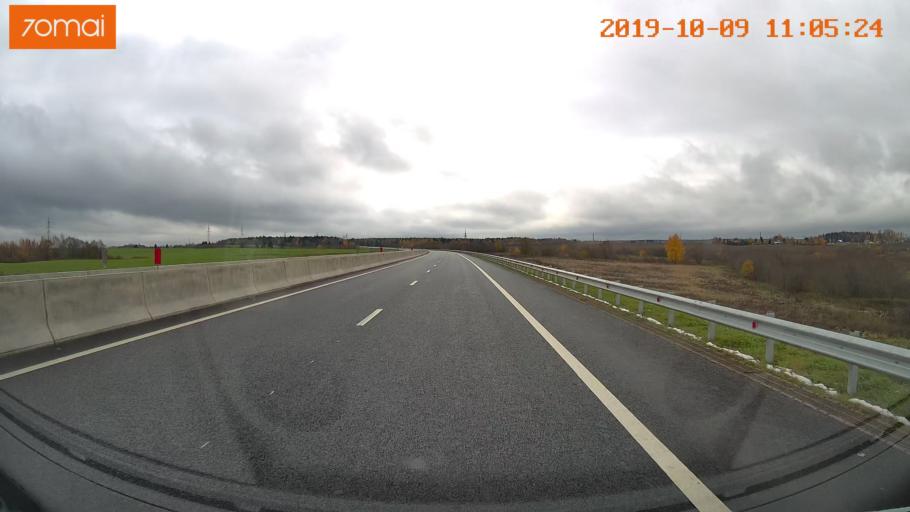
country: RU
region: Vologda
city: Molochnoye
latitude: 59.2006
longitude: 39.7592
